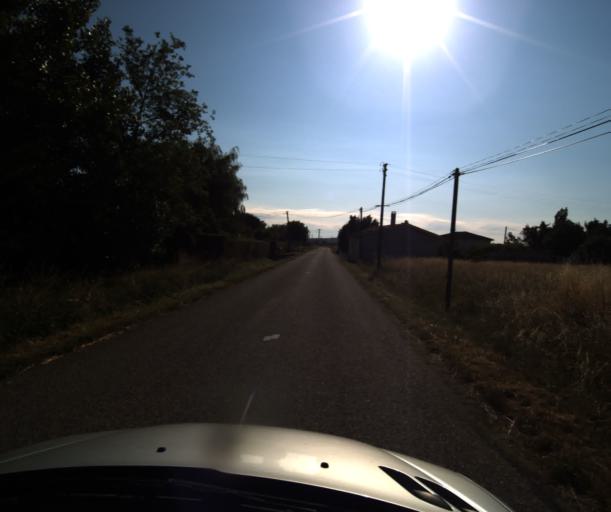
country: FR
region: Midi-Pyrenees
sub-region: Departement du Tarn-et-Garonne
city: Bressols
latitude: 43.9663
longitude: 1.2990
